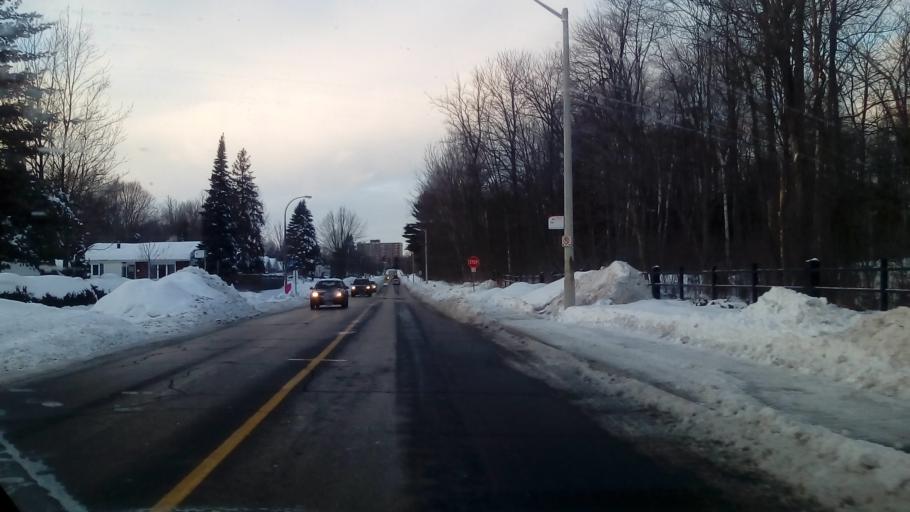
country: CA
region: Ontario
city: Ottawa
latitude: 45.4364
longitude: -75.6197
